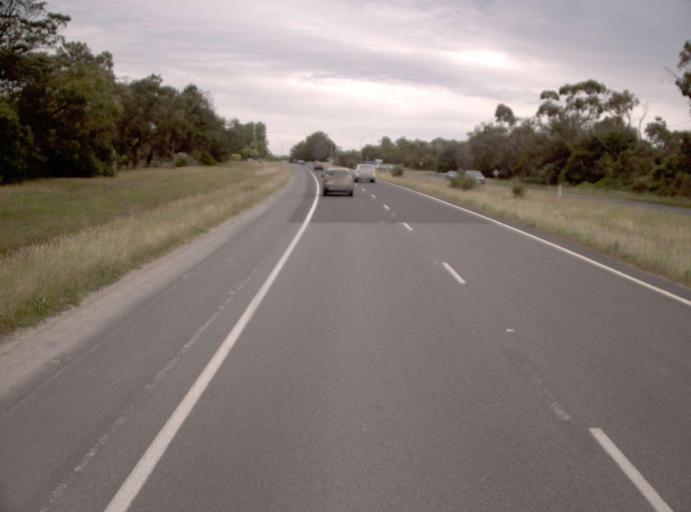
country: AU
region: Victoria
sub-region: Casey
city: Junction Village
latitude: -38.1298
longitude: 145.2923
